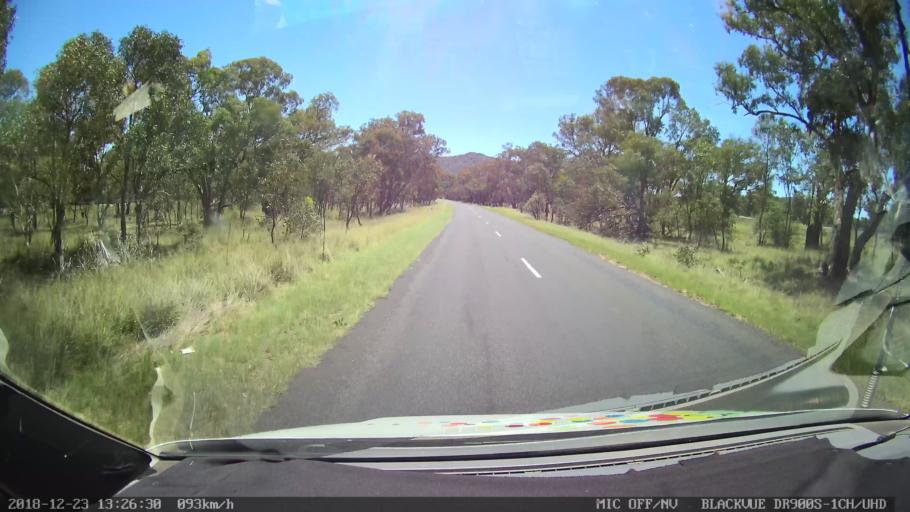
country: AU
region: New South Wales
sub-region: Armidale Dumaresq
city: Armidale
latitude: -30.4669
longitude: 151.3684
